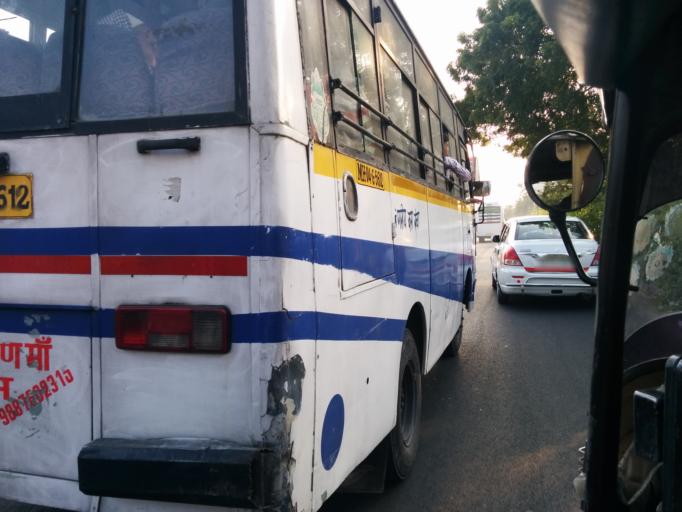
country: IN
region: Rajasthan
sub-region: Jaipur
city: Jaipur
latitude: 26.9584
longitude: 75.8441
